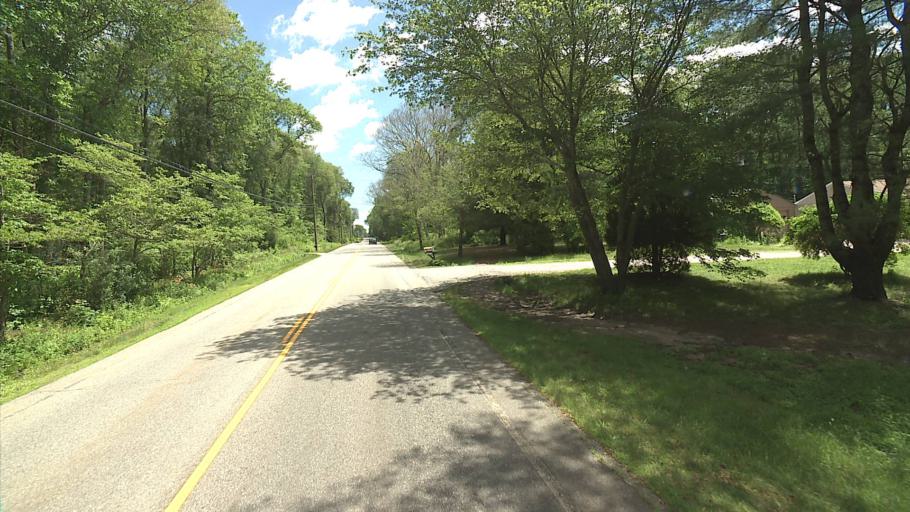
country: US
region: Connecticut
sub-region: New London County
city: Old Mystic
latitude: 41.4124
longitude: -71.9148
